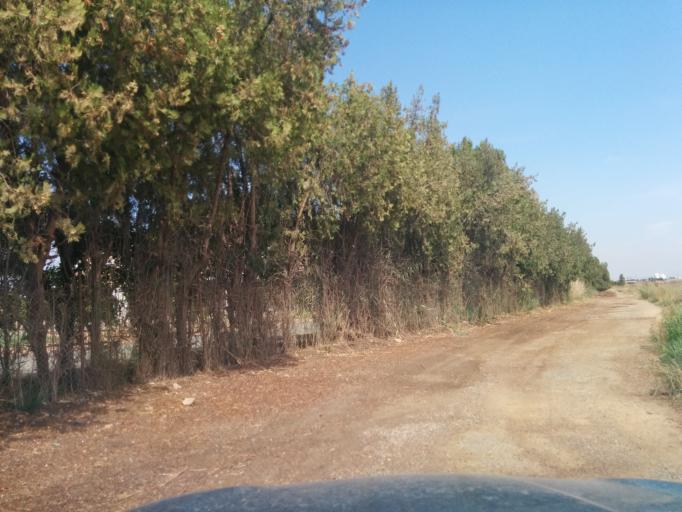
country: ES
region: Andalusia
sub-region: Provincia de Sevilla
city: Gelves
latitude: 37.3232
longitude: -5.9940
